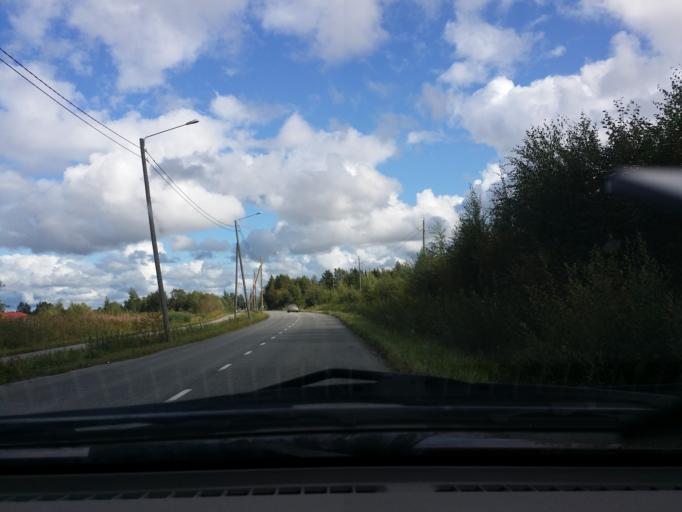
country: FI
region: Satakunta
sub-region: Pori
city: Pori
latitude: 61.4942
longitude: 21.8298
